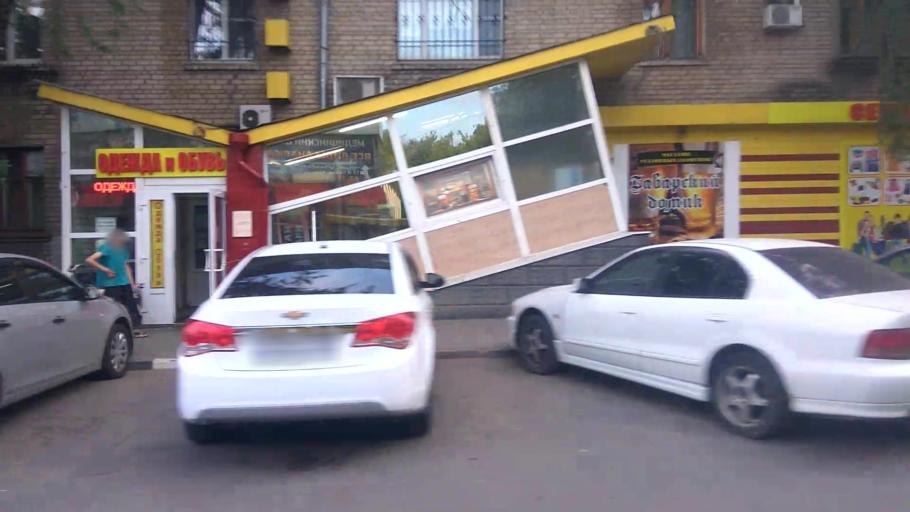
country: RU
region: Moskovskaya
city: Korolev
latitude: 55.9233
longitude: 37.7835
